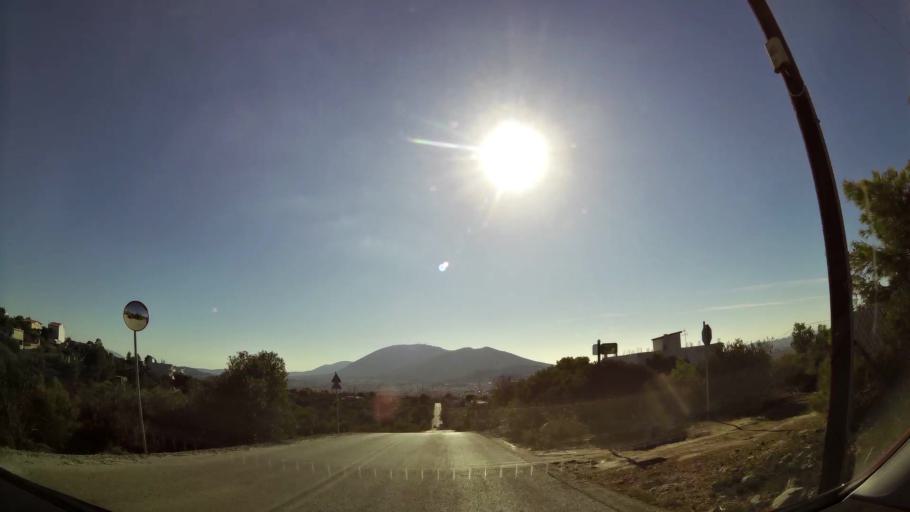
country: GR
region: Attica
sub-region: Nomarchia Anatolikis Attikis
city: Anthousa
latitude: 38.0317
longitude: 23.8725
